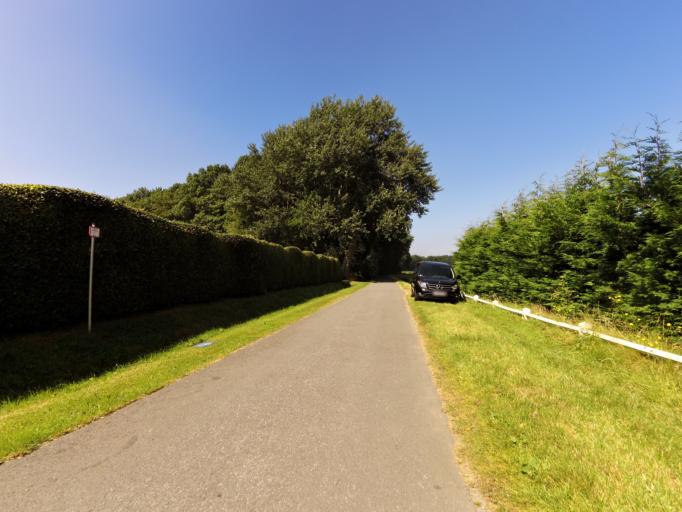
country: BE
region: Flanders
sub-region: Provincie West-Vlaanderen
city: Zedelgem
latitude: 51.1545
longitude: 3.1403
